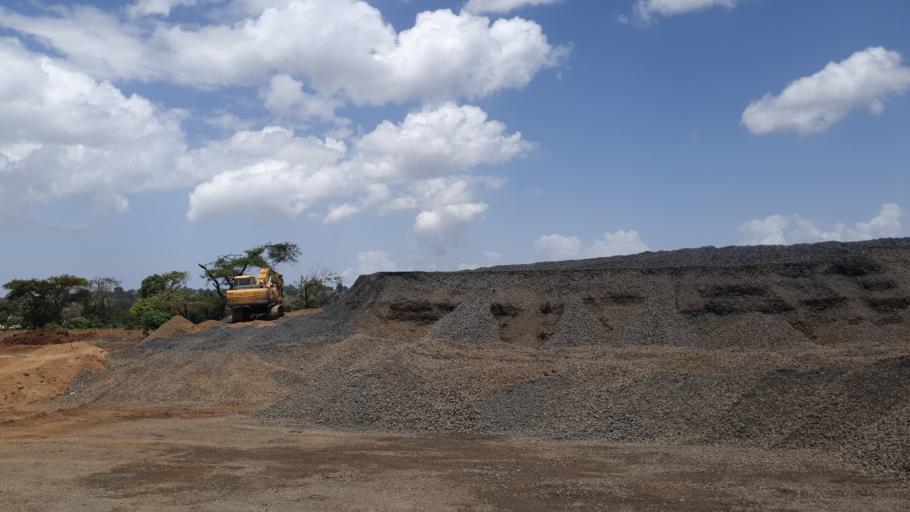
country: ET
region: Oromiya
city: Shambu
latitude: 10.0248
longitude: 36.8824
